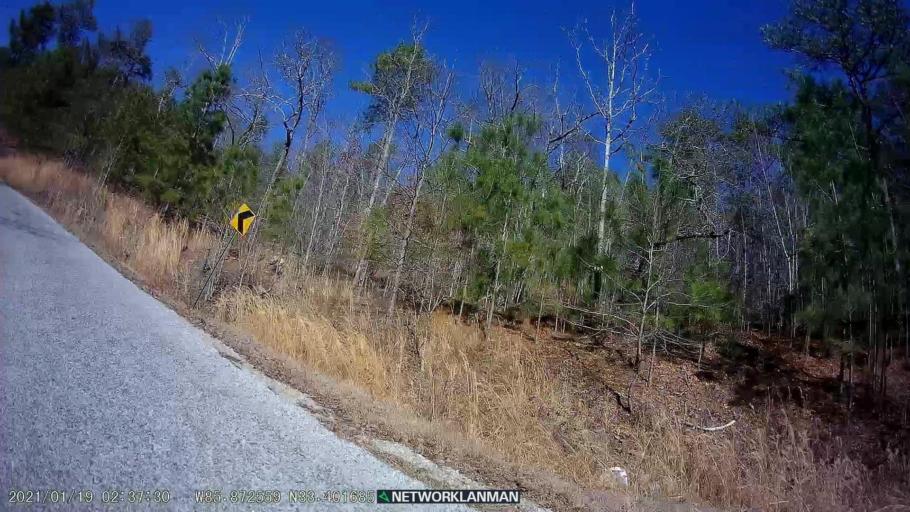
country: US
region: Alabama
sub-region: Clay County
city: Ashland
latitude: 33.4018
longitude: -85.8726
